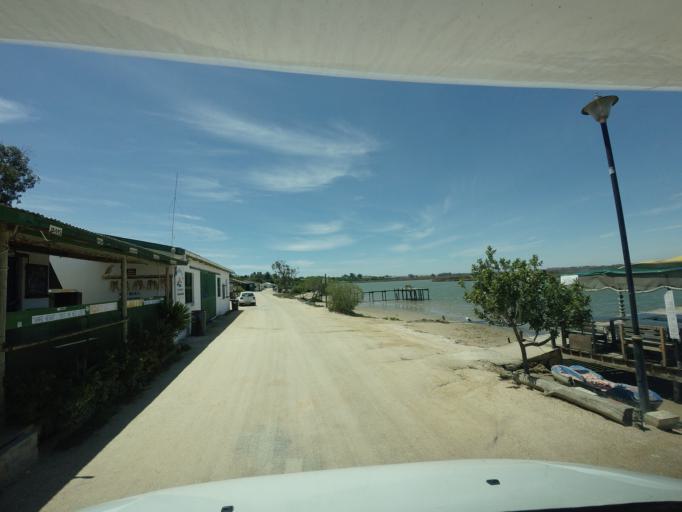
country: ZA
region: Western Cape
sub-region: West Coast District Municipality
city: Vredenburg
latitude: -32.7878
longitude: 18.1861
